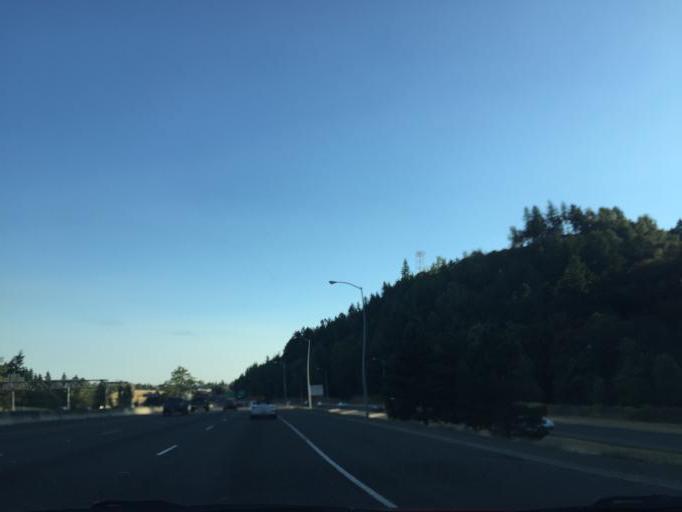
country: US
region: Oregon
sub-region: Multnomah County
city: Lents
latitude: 45.5448
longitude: -122.5612
